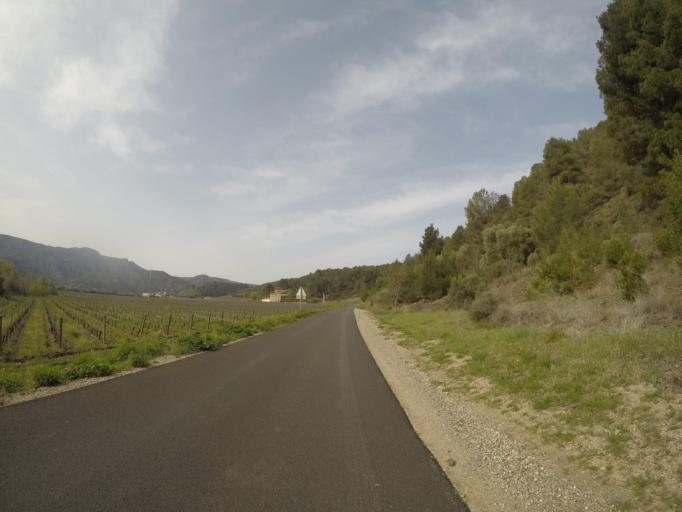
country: FR
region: Languedoc-Roussillon
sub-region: Departement des Pyrenees-Orientales
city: Baixas
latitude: 42.7847
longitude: 2.7694
